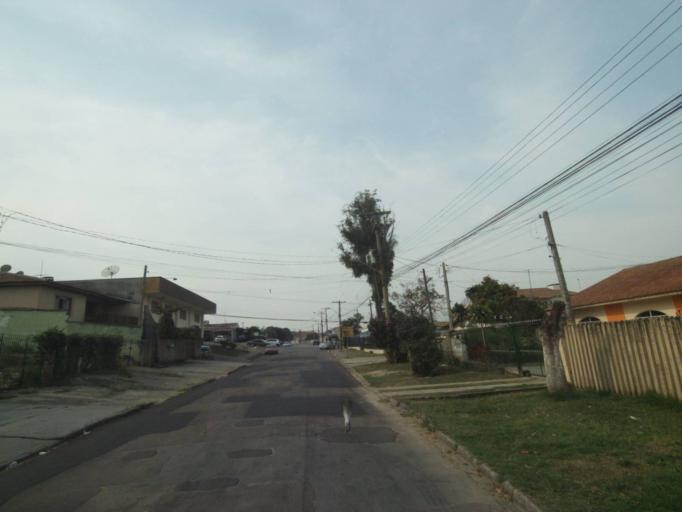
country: BR
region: Parana
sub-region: Sao Jose Dos Pinhais
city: Sao Jose dos Pinhais
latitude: -25.5216
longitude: -49.2735
